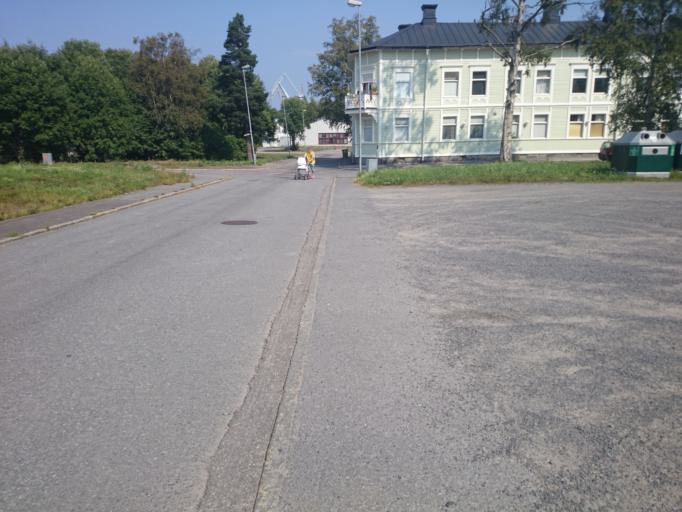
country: SE
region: Vaesternorrland
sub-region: Haernoesands Kommun
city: Haernoesand
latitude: 62.6359
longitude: 17.9324
